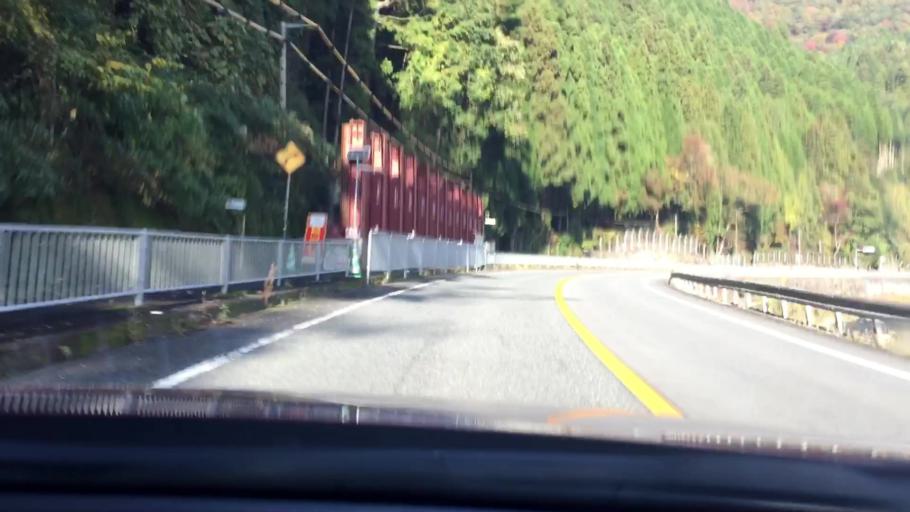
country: JP
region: Hyogo
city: Yamazakicho-nakabirose
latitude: 35.1429
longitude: 134.5410
